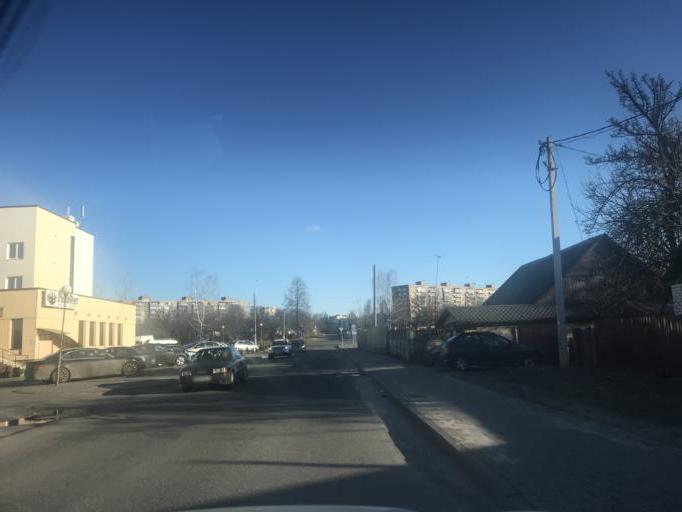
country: BY
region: Mogilev
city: Mahilyow
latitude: 53.9098
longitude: 30.3568
